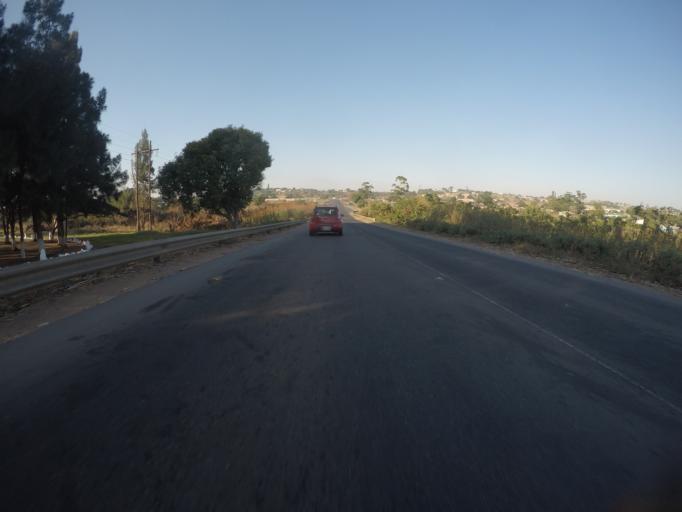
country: ZA
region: KwaZulu-Natal
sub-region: iLembe District Municipality
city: Stanger
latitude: -29.3959
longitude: 31.2517
